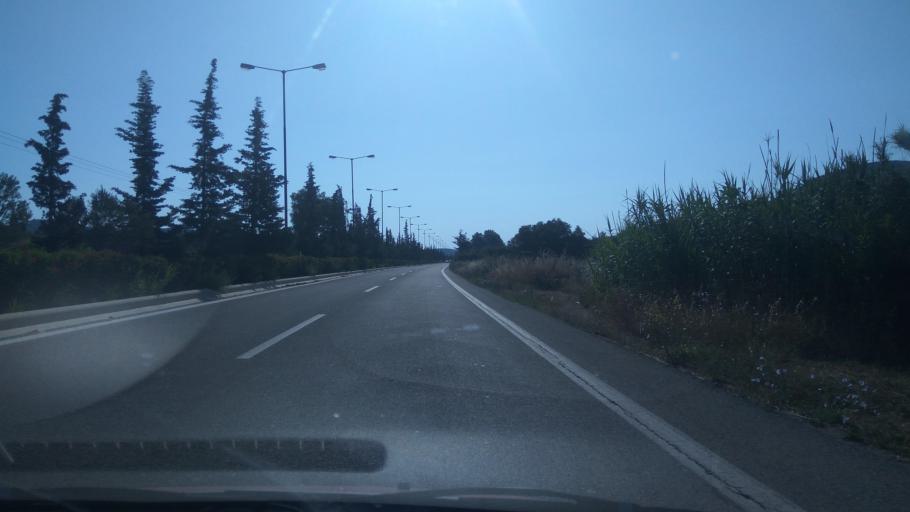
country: GR
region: Attica
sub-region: Nomarchia Anatolikis Attikis
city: Keratea
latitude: 37.8013
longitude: 24.0116
